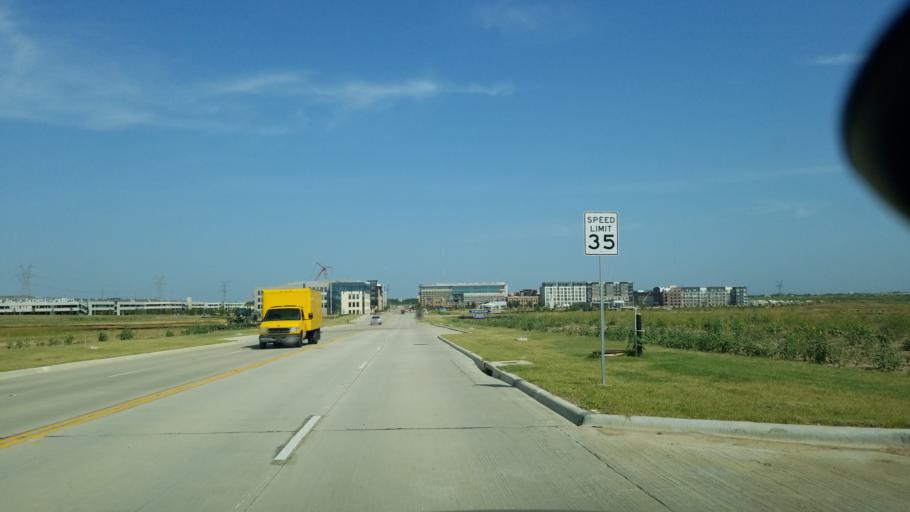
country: US
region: Texas
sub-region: Dallas County
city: Coppell
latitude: 32.9327
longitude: -96.9778
